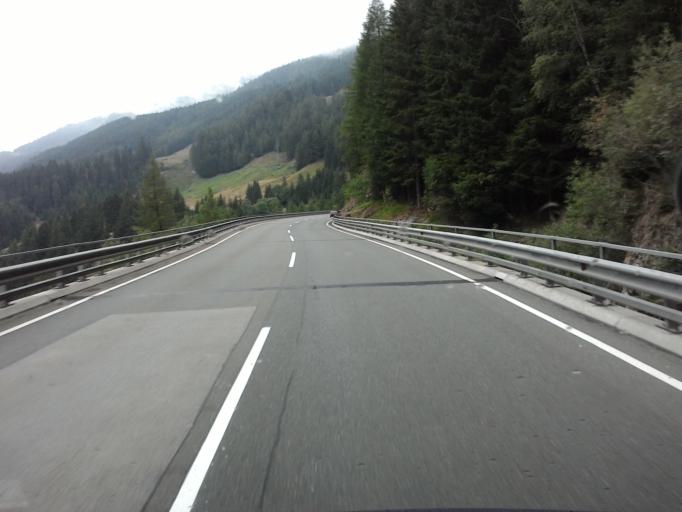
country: AT
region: Tyrol
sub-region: Politischer Bezirk Lienz
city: Matrei in Osttirol
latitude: 47.0853
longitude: 12.5305
